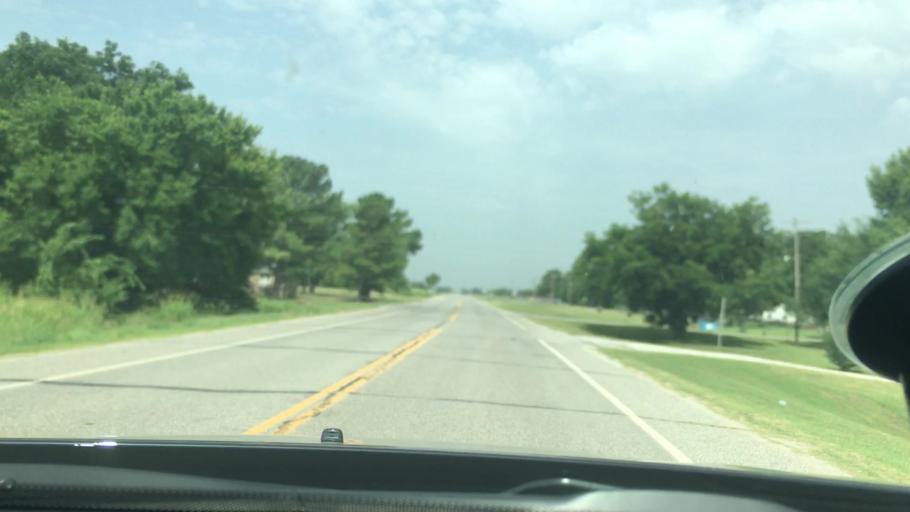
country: US
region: Oklahoma
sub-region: Garvin County
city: Pauls Valley
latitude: 34.8262
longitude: -97.2644
